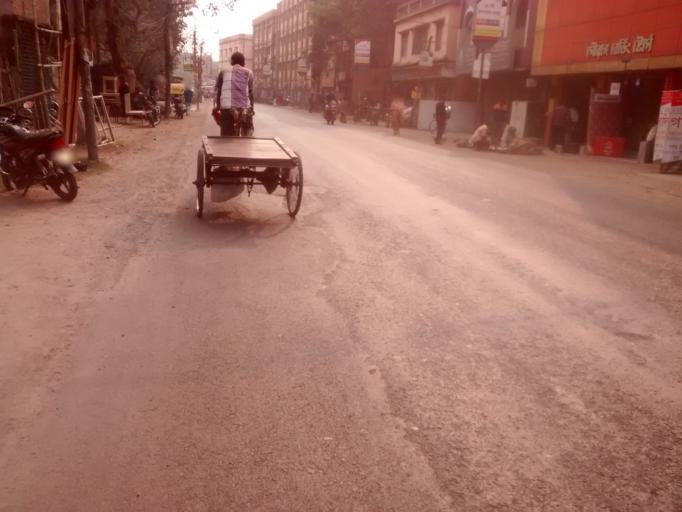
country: IN
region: West Bengal
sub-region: North 24 Parganas
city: Barasat
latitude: 22.7176
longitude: 88.4759
